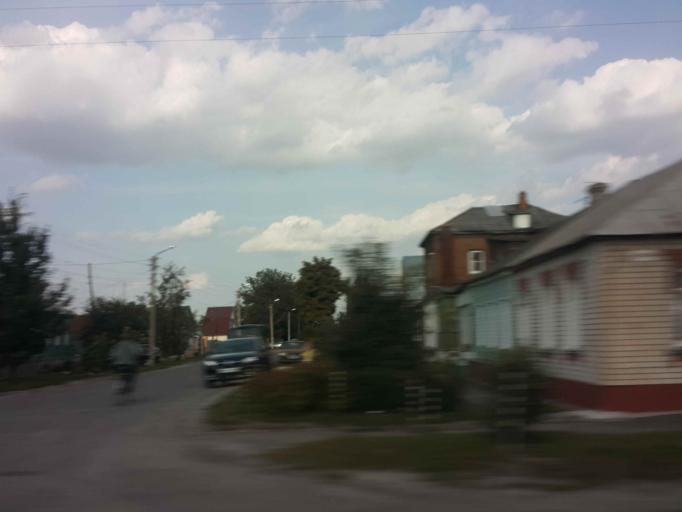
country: RU
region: Tambov
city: Tambov
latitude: 52.7155
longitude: 41.4393
